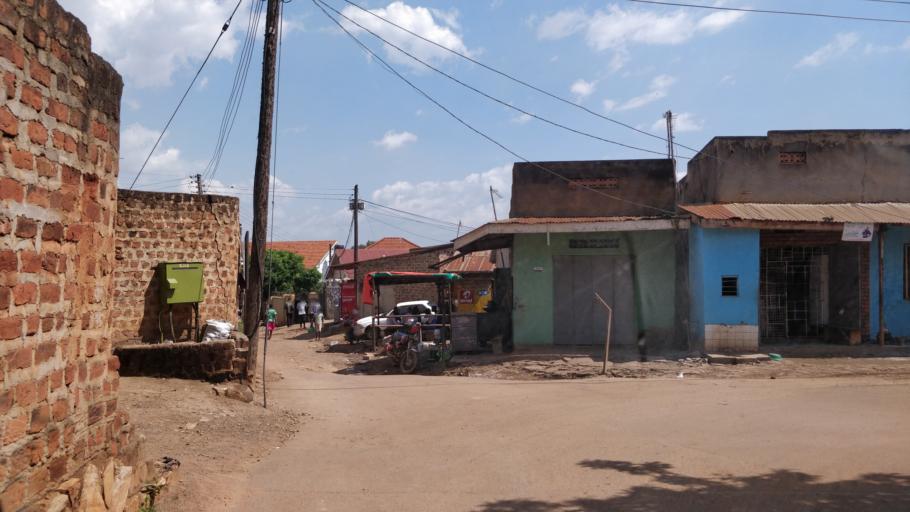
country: UG
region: Central Region
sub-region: Kampala District
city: Kampala
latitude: 0.2846
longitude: 32.6177
